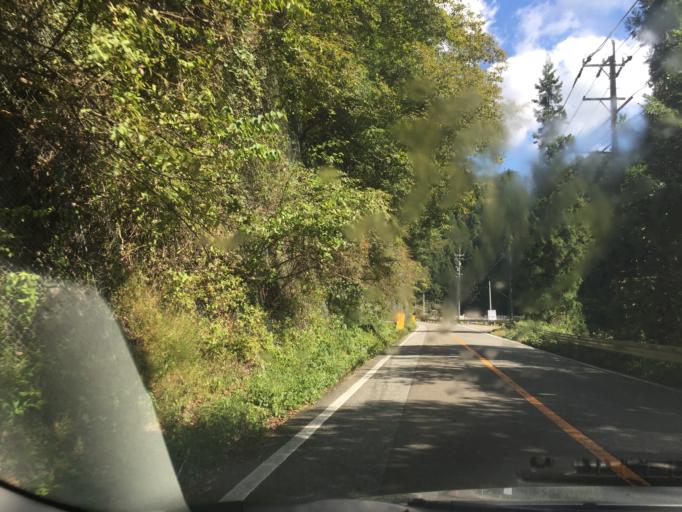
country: JP
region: Aichi
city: Shinshiro
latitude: 35.1352
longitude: 137.6853
